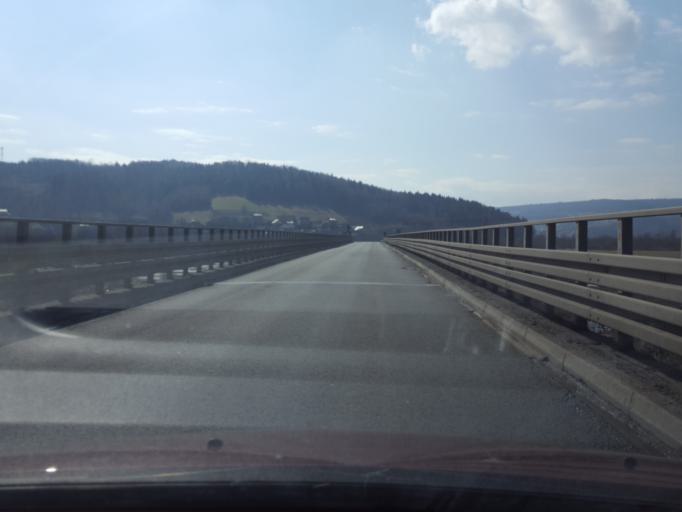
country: PL
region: Lesser Poland Voivodeship
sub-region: Powiat nowosadecki
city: Chelmiec
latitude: 49.6893
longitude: 20.6547
